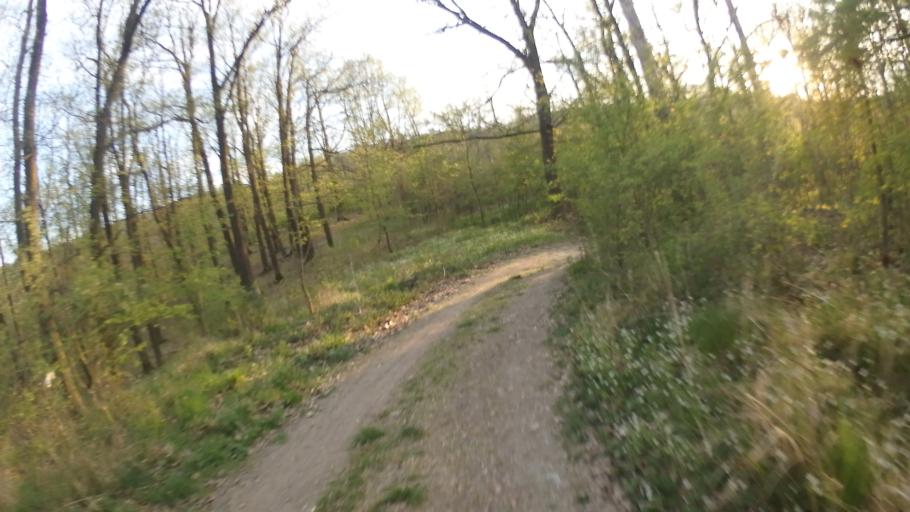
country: CZ
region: South Moravian
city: Zelesice
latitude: 49.1265
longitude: 16.5576
